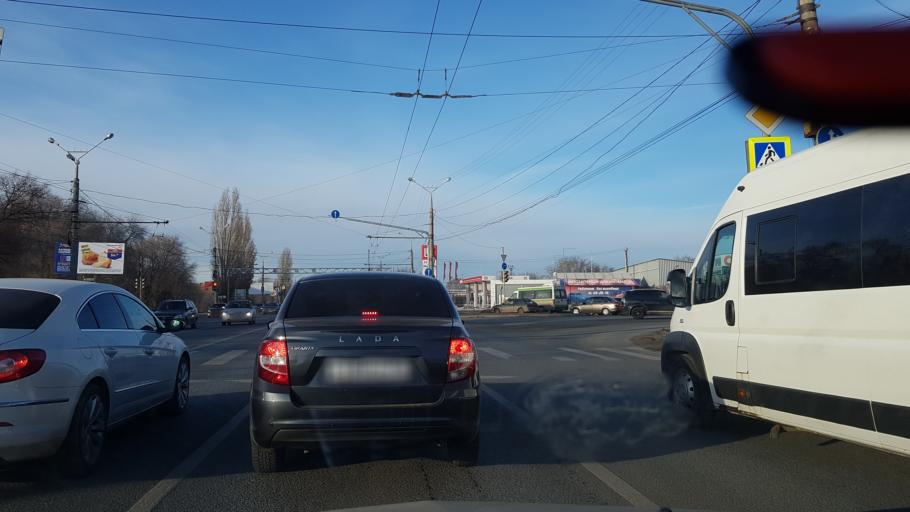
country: RU
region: Samara
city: Tol'yatti
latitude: 53.5355
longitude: 49.3947
